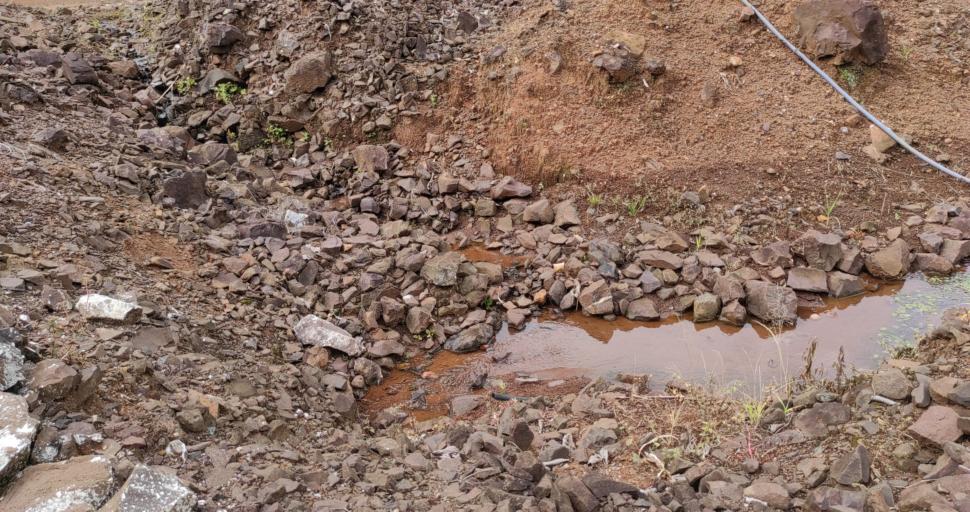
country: AR
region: Misiones
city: Puerto Libertad
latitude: -25.9579
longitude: -54.5993
